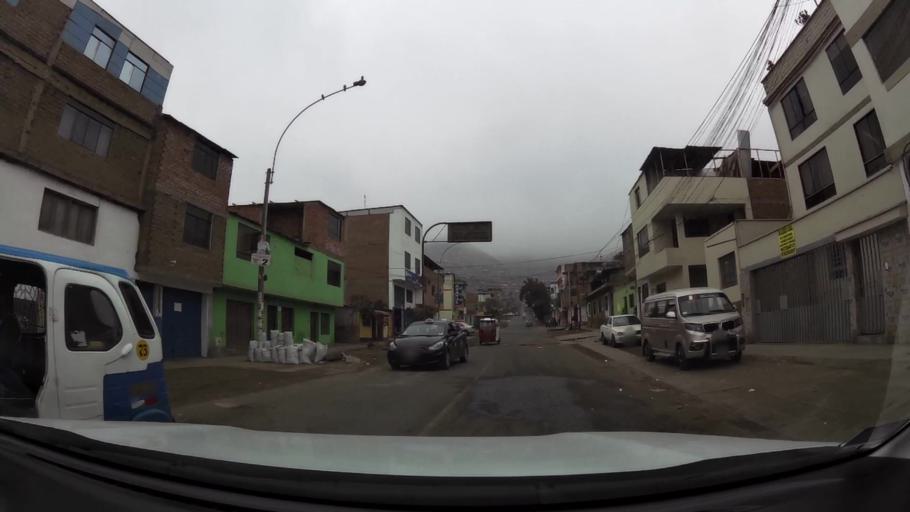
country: PE
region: Lima
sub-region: Lima
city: Surco
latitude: -12.1707
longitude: -76.9459
